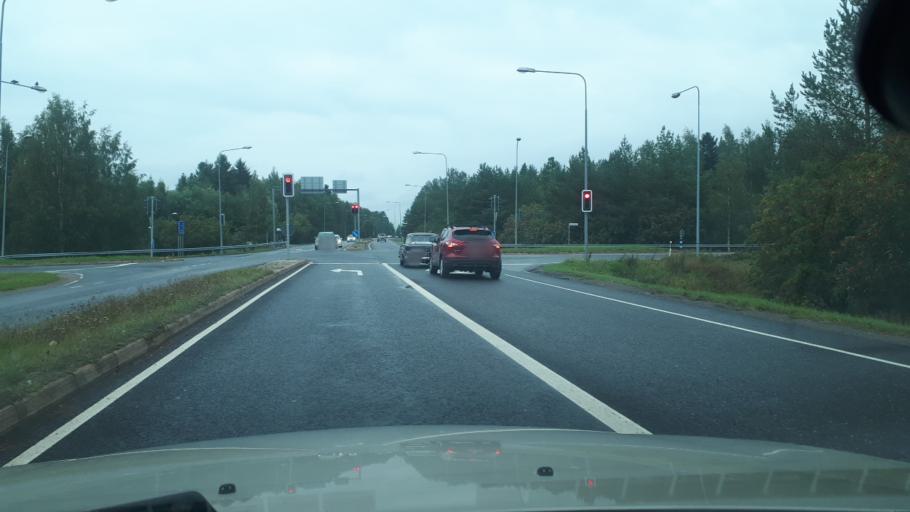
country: FI
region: Northern Ostrobothnia
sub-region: Oulu
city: Haukipudas
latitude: 65.1661
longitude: 25.3473
